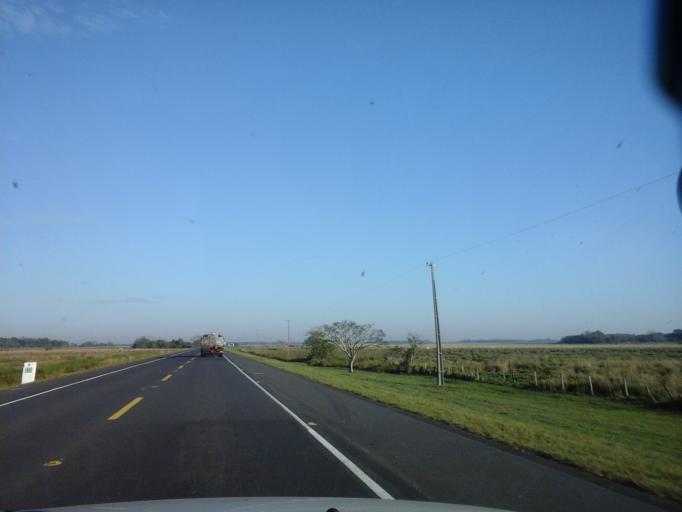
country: PY
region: Neembucu
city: Pilar
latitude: -26.8718
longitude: -57.9214
